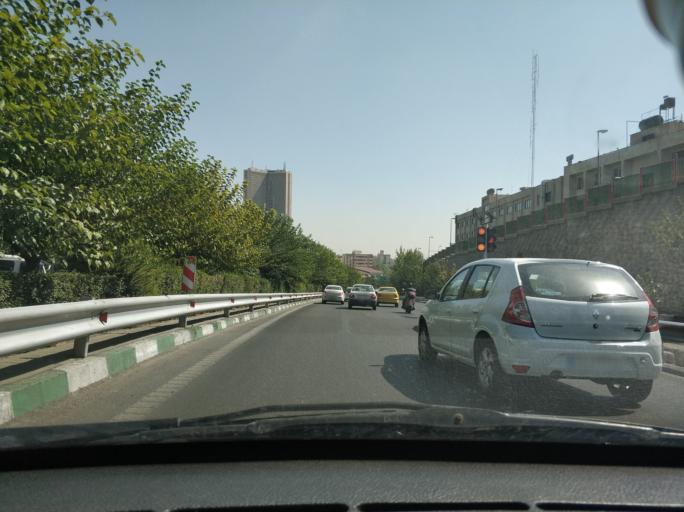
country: IR
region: Tehran
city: Tehran
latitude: 35.7432
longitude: 51.3881
